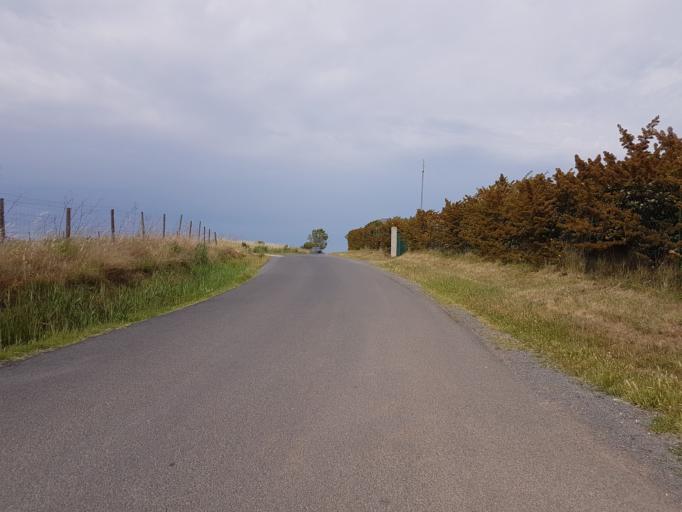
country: FR
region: Languedoc-Roussillon
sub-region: Departement de l'Herault
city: Portiragnes
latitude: 43.3108
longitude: 3.3579
